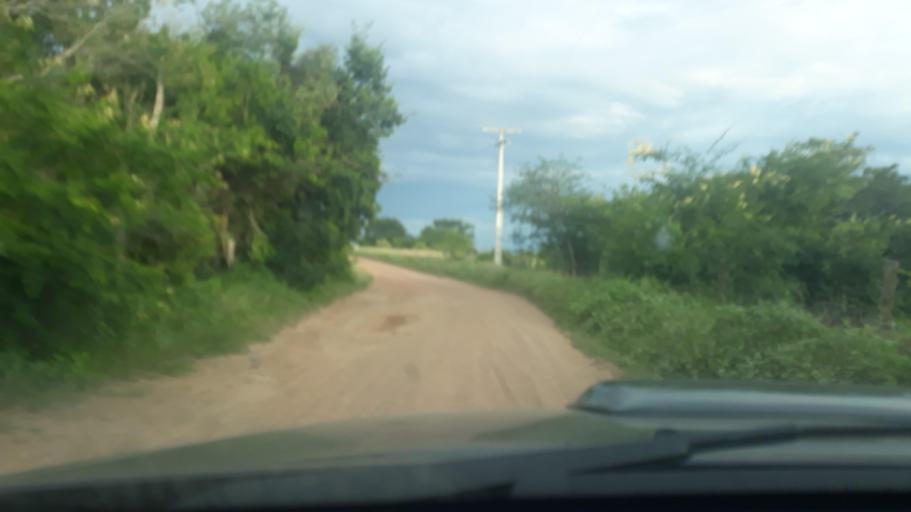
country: BR
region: Bahia
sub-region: Riacho De Santana
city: Riacho de Santana
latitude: -13.9049
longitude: -42.9773
